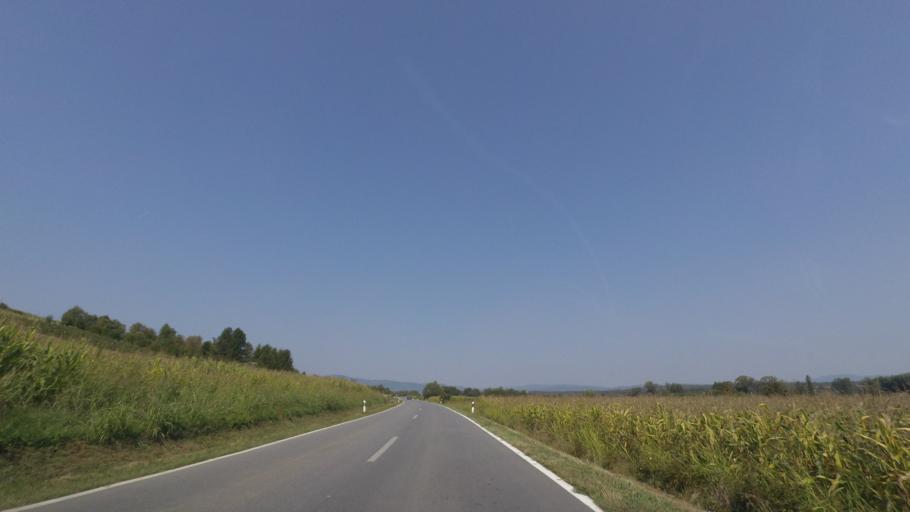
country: HR
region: Pozesko-Slavonska
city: Pozega
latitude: 45.3364
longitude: 17.5899
